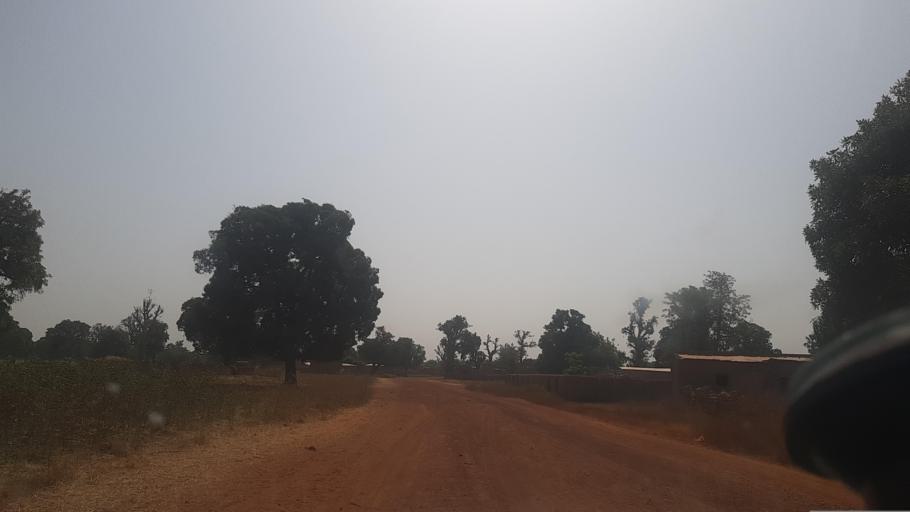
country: ML
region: Segou
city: Baroueli
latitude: 13.0149
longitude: -6.4242
